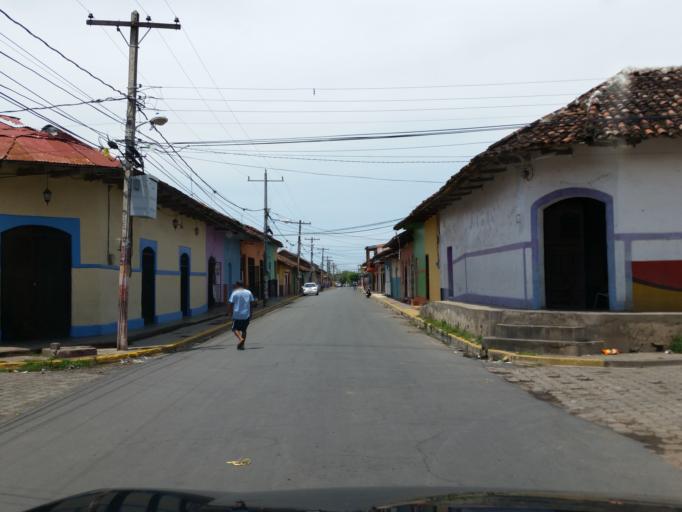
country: NI
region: Granada
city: Granada
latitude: 11.9339
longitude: -85.9527
